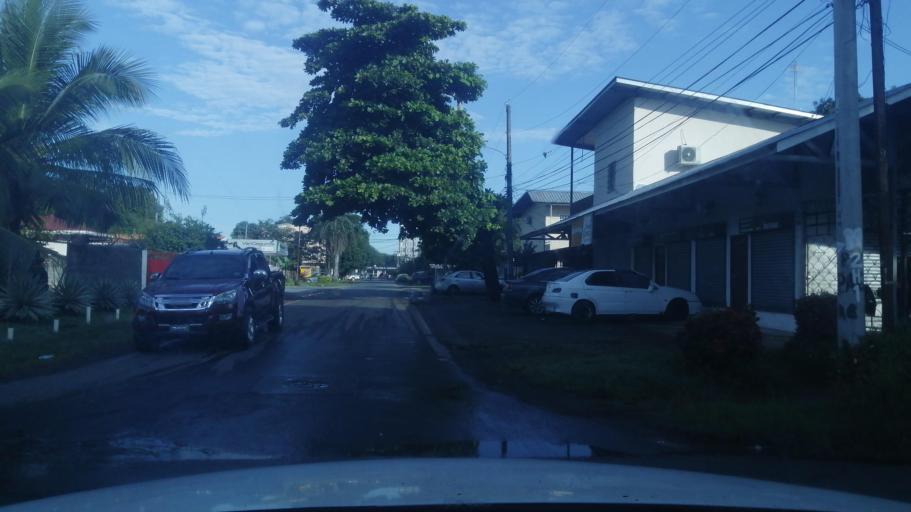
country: PA
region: Chiriqui
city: David
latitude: 8.4249
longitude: -82.4352
